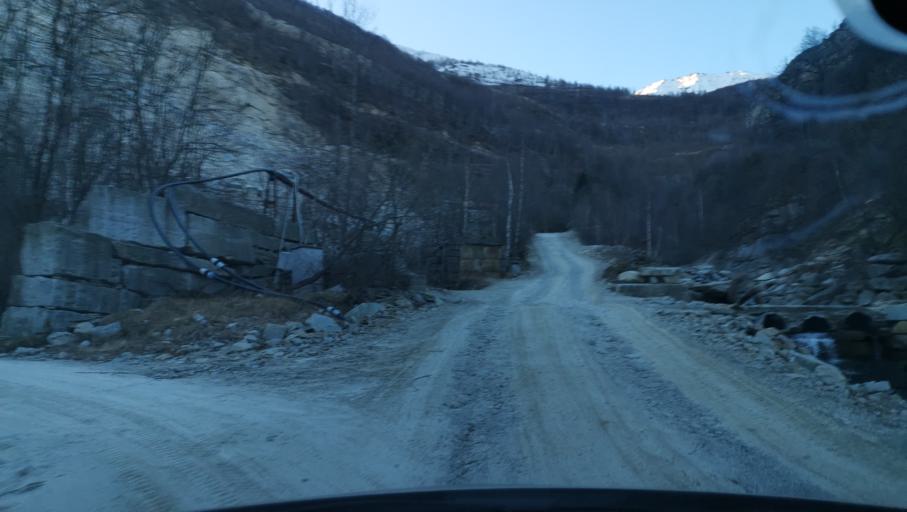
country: IT
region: Piedmont
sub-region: Provincia di Torino
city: Rora
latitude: 44.7629
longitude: 7.2006
